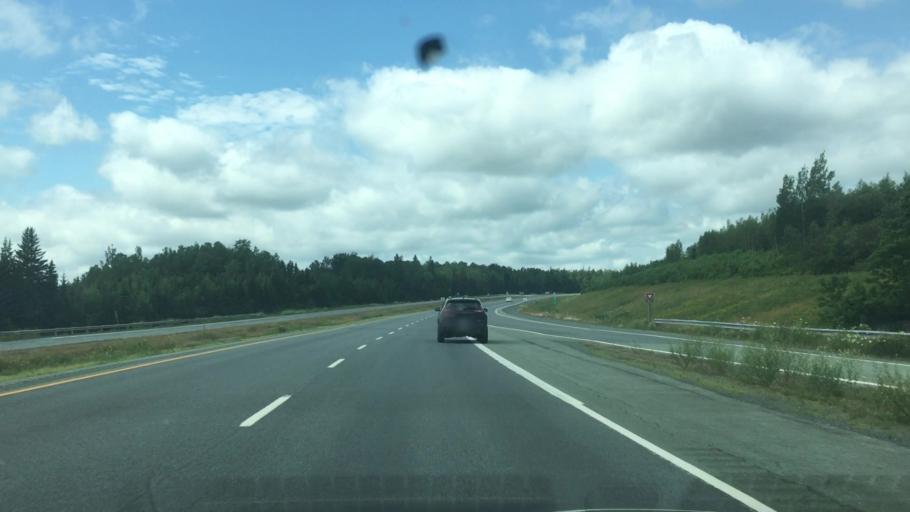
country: CA
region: Nova Scotia
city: Springhill
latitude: 45.6922
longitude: -64.0067
